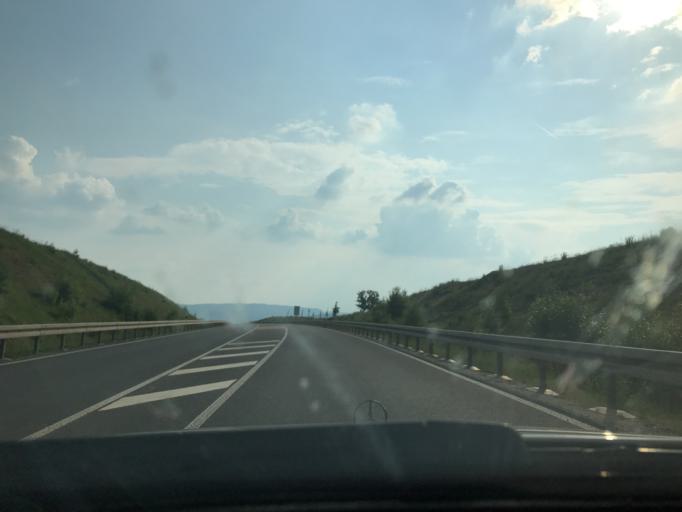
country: DE
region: Thuringia
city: Heilbad Heiligenstadt
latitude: 51.3873
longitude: 10.1205
